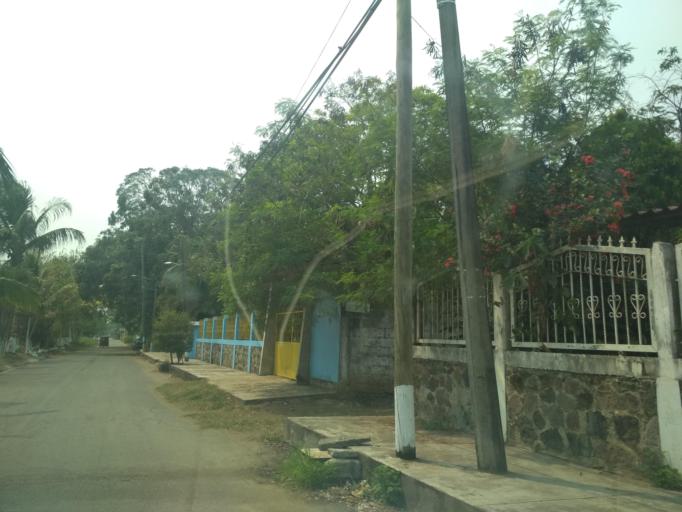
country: MX
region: Veracruz
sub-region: Veracruz
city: Delfino Victoria (Santa Fe)
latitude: 19.2058
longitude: -96.2714
